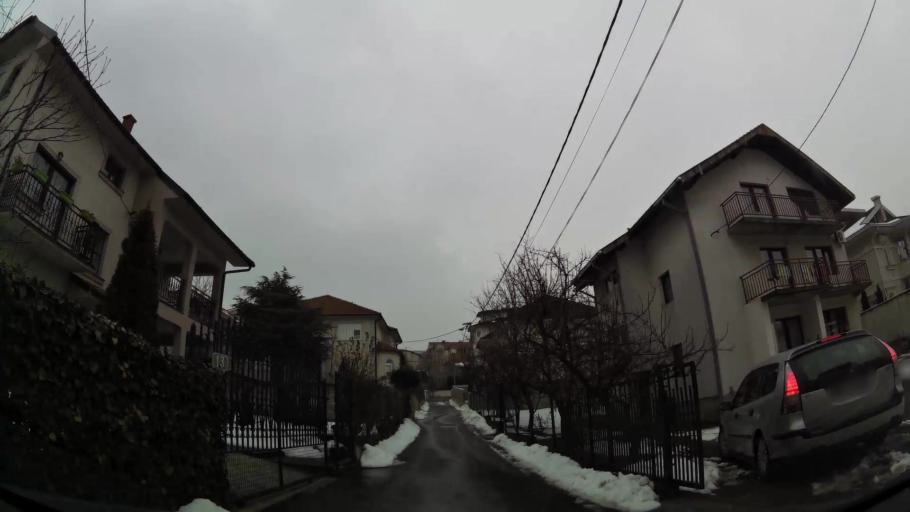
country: RS
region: Central Serbia
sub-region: Belgrade
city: Vozdovac
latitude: 44.7631
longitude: 20.5006
